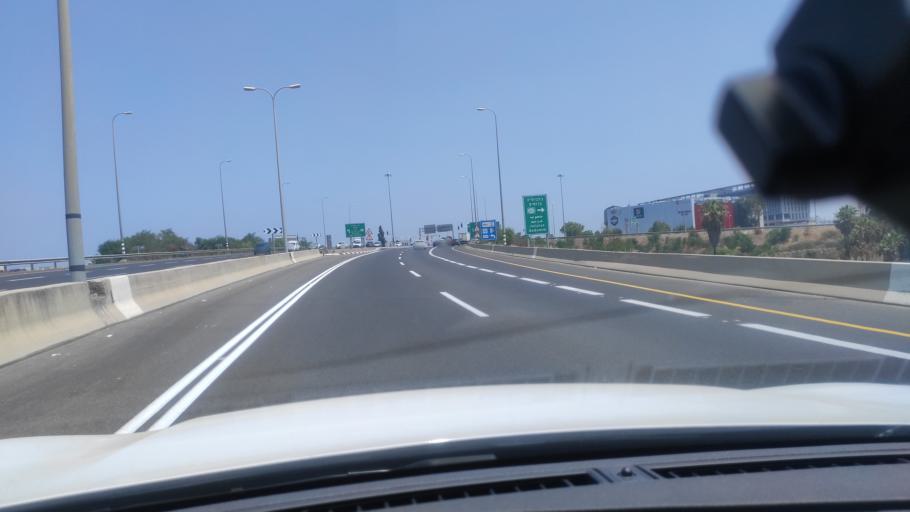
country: IL
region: Central District
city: Kfar Saba
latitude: 32.1616
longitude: 34.9260
